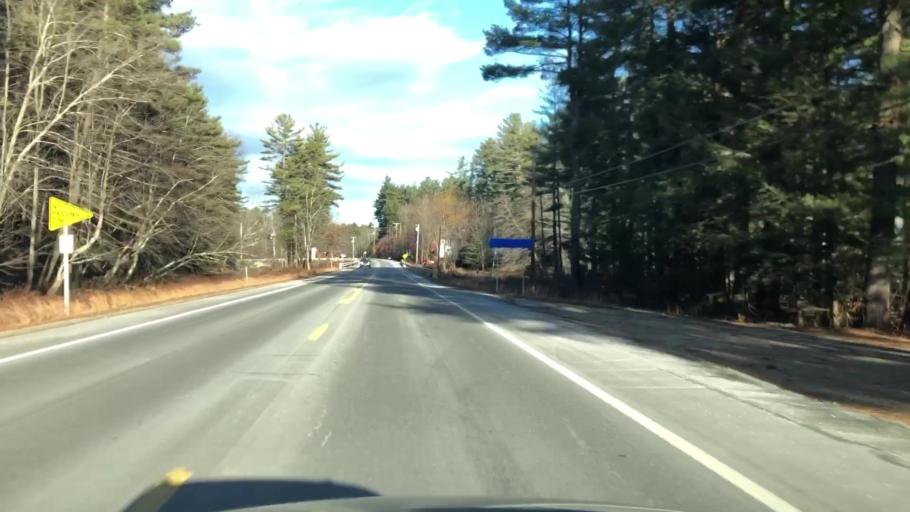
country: US
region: New Hampshire
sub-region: Hillsborough County
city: Brookline
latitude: 42.7079
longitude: -71.6693
